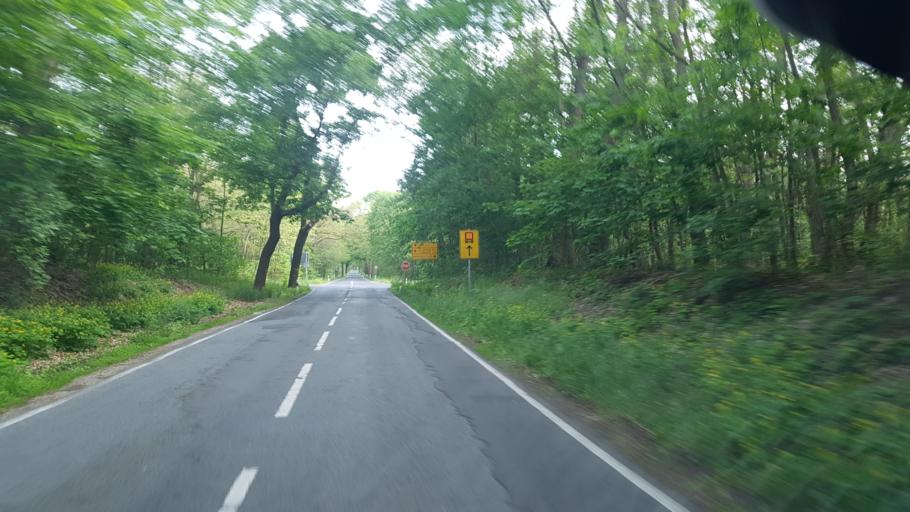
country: DE
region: Brandenburg
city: Baruth
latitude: 52.0247
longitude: 13.4694
